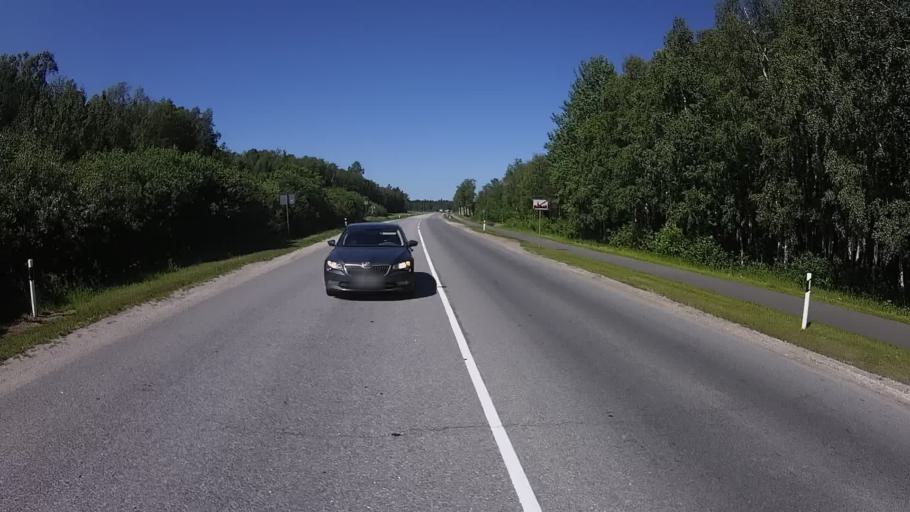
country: EE
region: Ida-Virumaa
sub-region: Kohtla-Jaerve linn
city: Kohtla-Jarve
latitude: 59.4151
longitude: 27.2755
